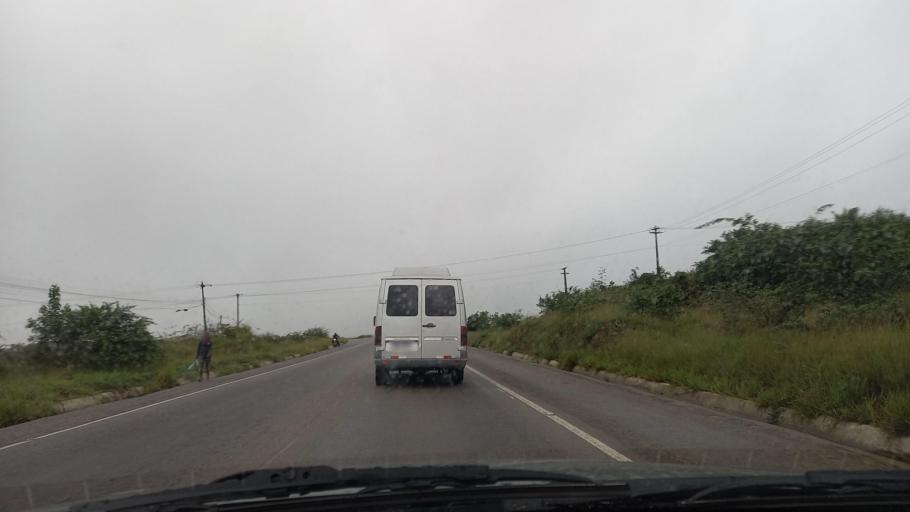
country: BR
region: Pernambuco
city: Garanhuns
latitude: -8.8723
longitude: -36.5079
